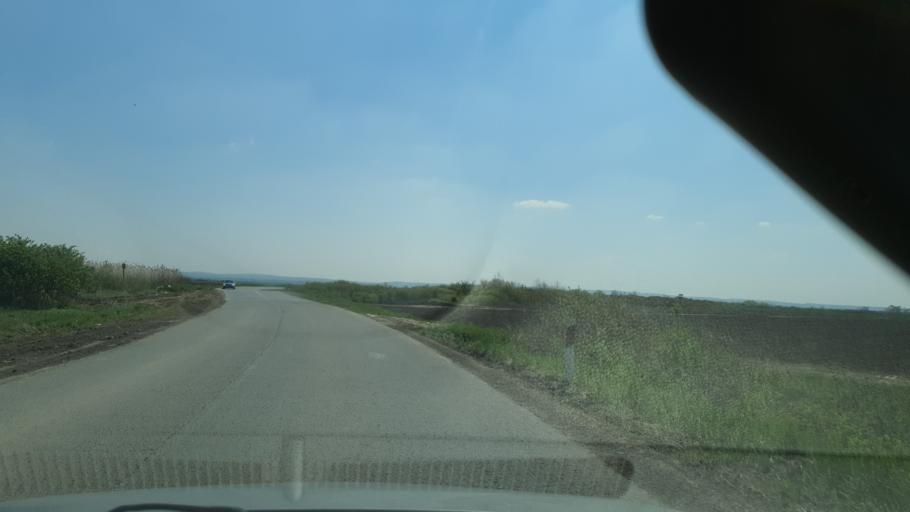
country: RS
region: Autonomna Pokrajina Vojvodina
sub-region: Juznobacki Okrug
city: Backa Palanka
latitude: 45.3154
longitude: 19.4412
